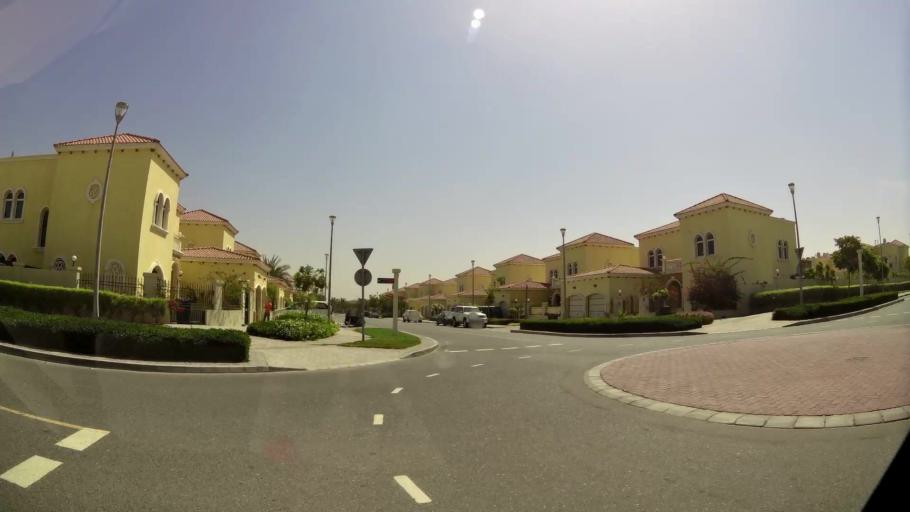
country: AE
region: Dubai
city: Dubai
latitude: 25.0509
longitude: 55.1464
